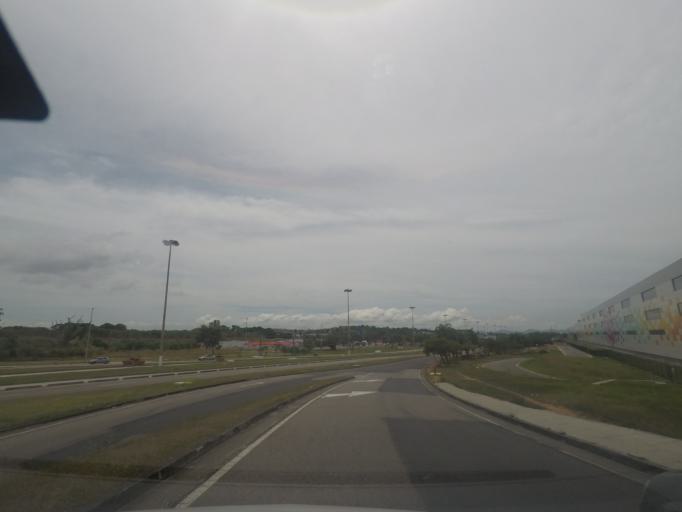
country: BR
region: Rio de Janeiro
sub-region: Duque De Caxias
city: Duque de Caxias
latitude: -22.8144
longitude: -43.2445
